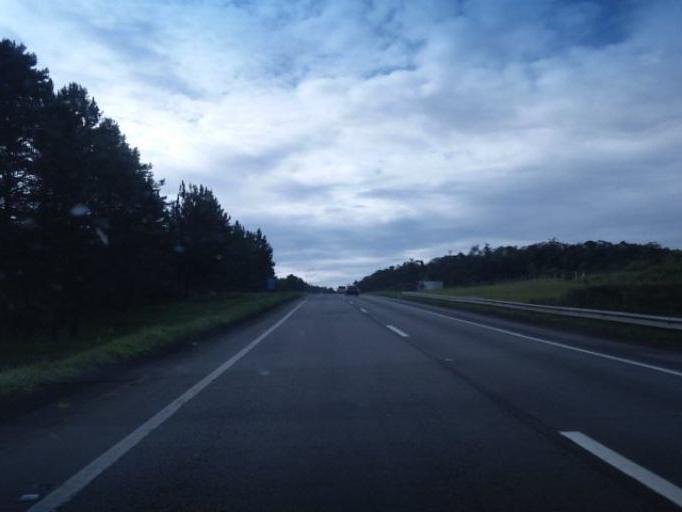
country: BR
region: Parana
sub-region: Campina Grande Do Sul
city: Campina Grande do Sul
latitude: -25.1068
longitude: -48.8040
